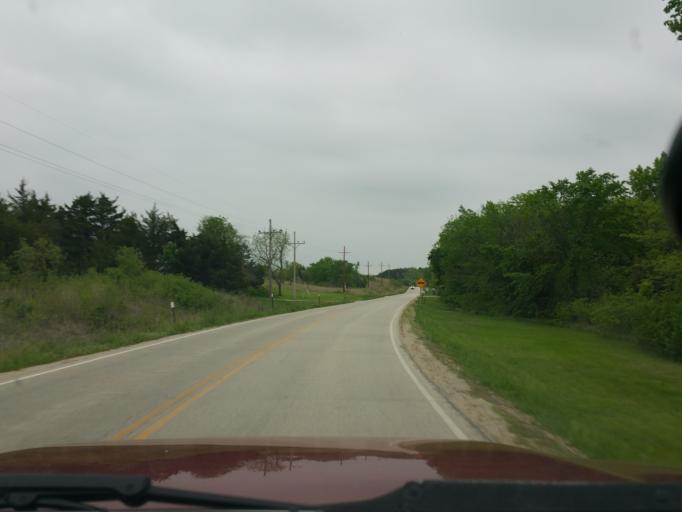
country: US
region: Kansas
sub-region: Riley County
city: Manhattan
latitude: 39.2632
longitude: -96.5702
